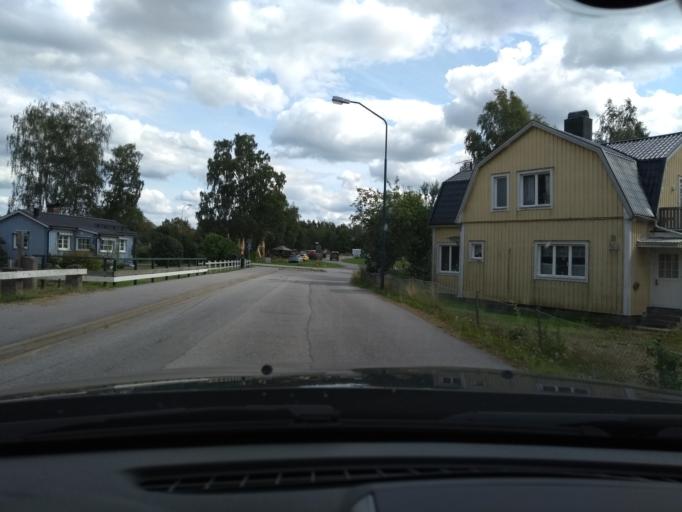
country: SE
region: Kalmar
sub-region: Vimmerby Kommun
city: Vimmerby
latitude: 57.6597
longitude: 15.8691
